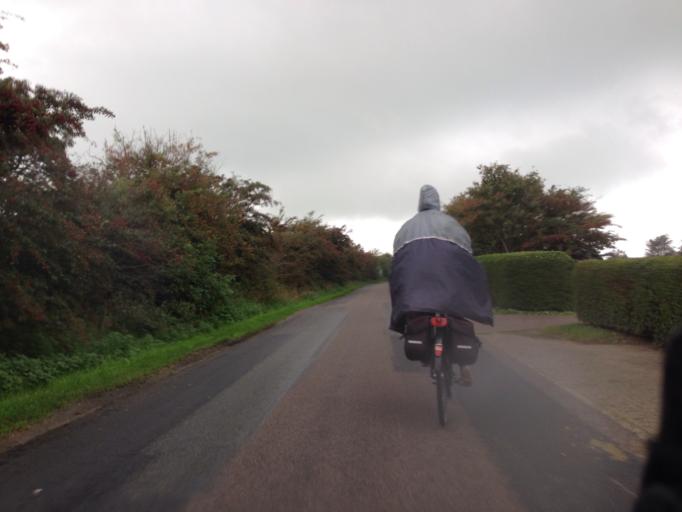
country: DE
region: Schleswig-Holstein
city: Midlum
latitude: 54.7119
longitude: 8.5215
